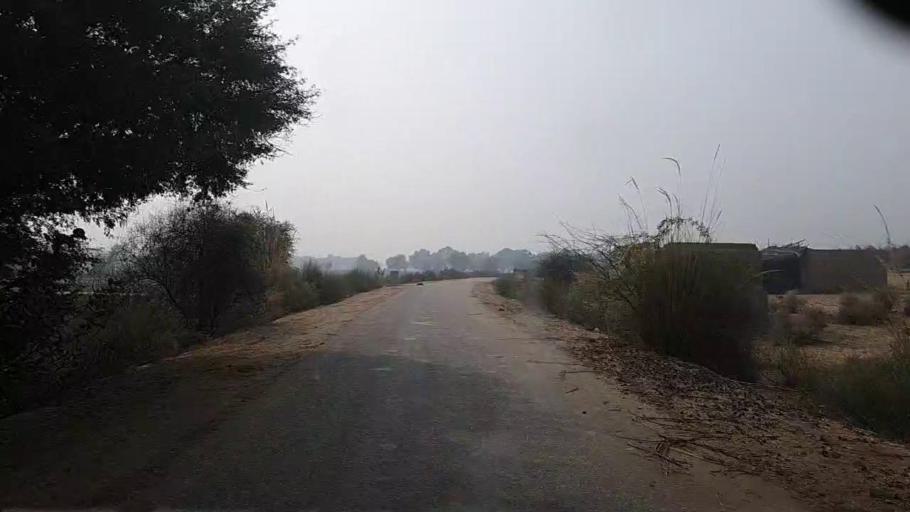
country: PK
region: Sindh
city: Kandiari
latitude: 26.9794
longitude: 68.6005
